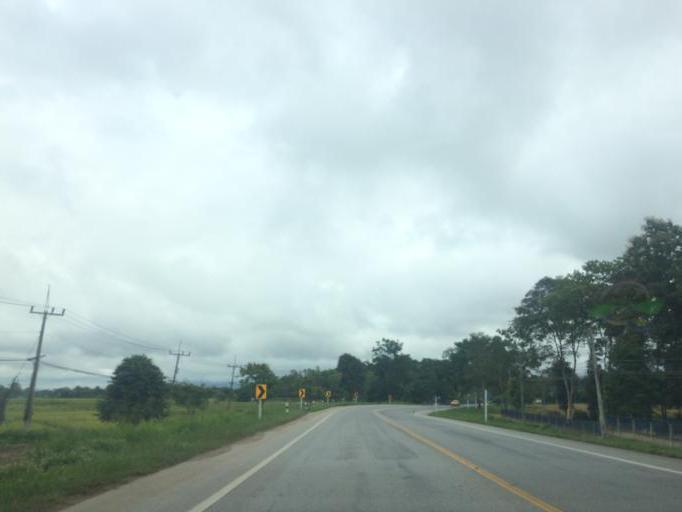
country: TH
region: Chiang Rai
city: Mae Lao
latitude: 19.7478
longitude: 99.6795
